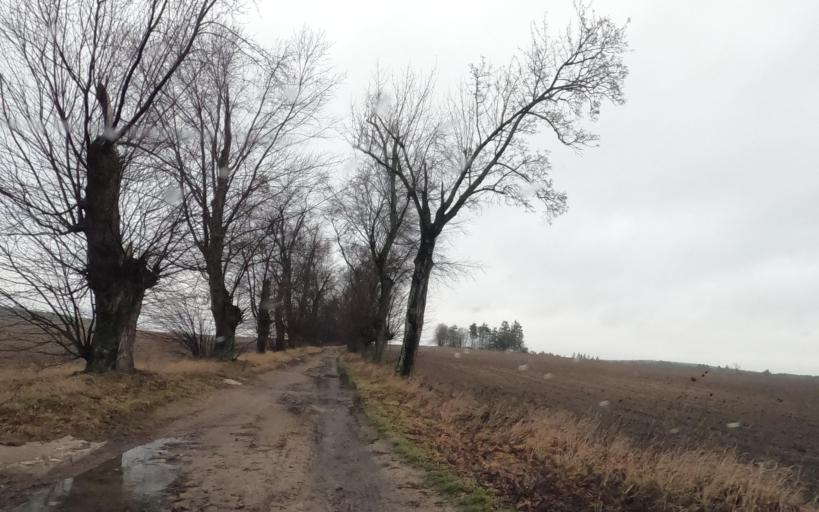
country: PL
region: West Pomeranian Voivodeship
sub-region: Powiat szczecinecki
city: Szczecinek
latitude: 53.6174
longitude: 16.6714
